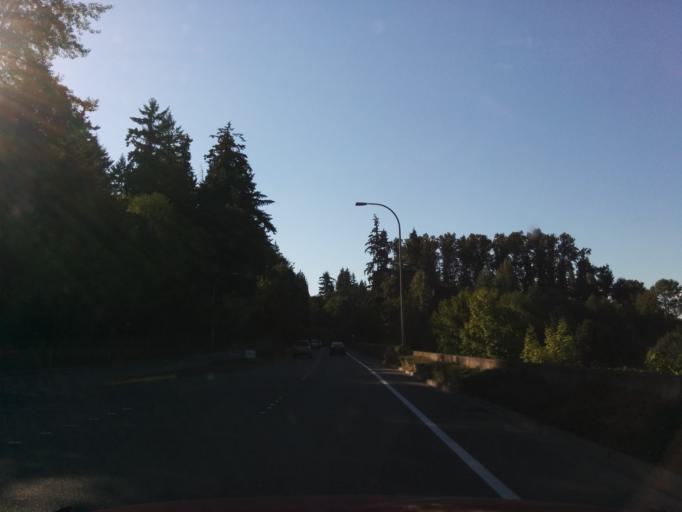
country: US
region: Washington
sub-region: King County
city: Redmond
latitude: 47.6594
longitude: -122.1233
